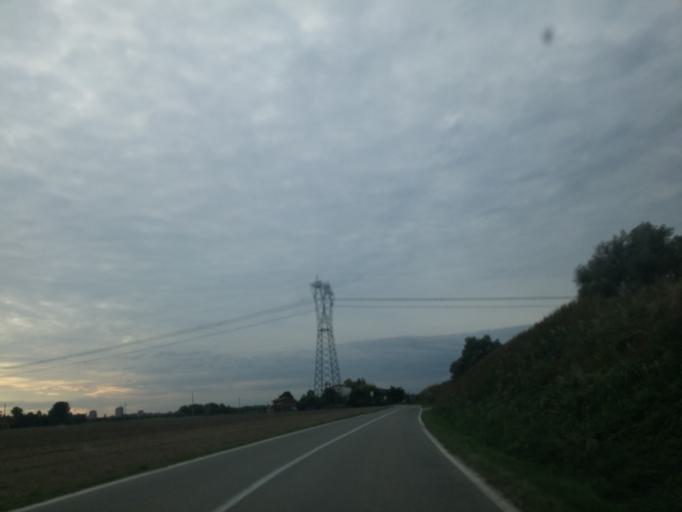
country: IT
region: Emilia-Romagna
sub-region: Provincia di Bologna
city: Longara
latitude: 44.5893
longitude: 11.3197
